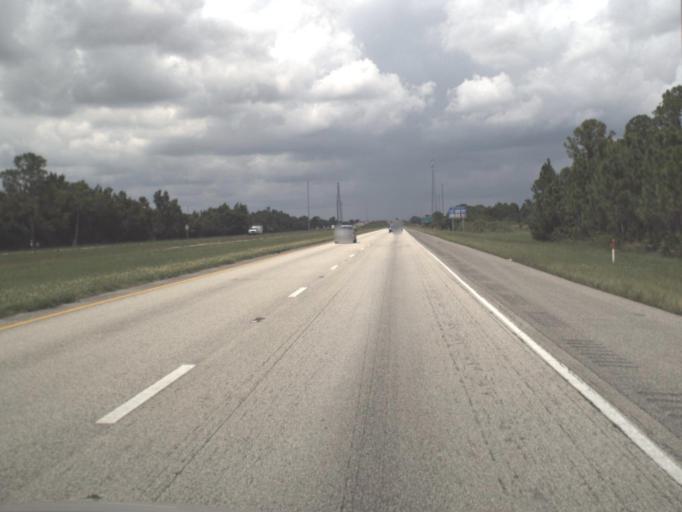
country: US
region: Florida
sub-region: Charlotte County
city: Harbour Heights
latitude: 27.0111
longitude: -82.0426
